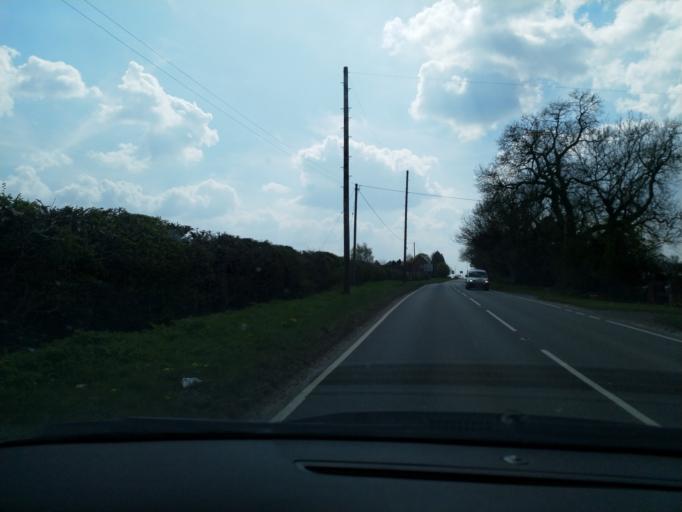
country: GB
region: England
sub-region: Warwickshire
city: Royal Leamington Spa
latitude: 52.3191
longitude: -1.5152
